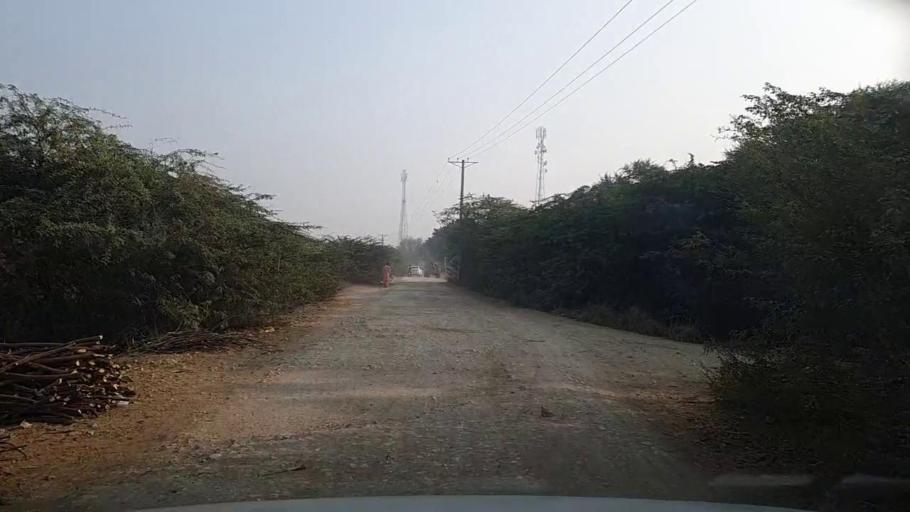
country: PK
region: Sindh
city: Kandiari
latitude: 27.0322
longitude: 68.4860
